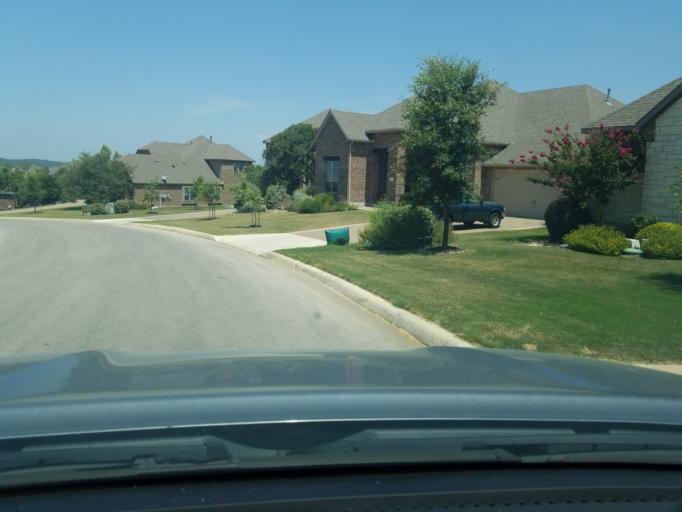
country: US
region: Texas
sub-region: Bexar County
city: Timberwood Park
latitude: 29.7109
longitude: -98.5033
